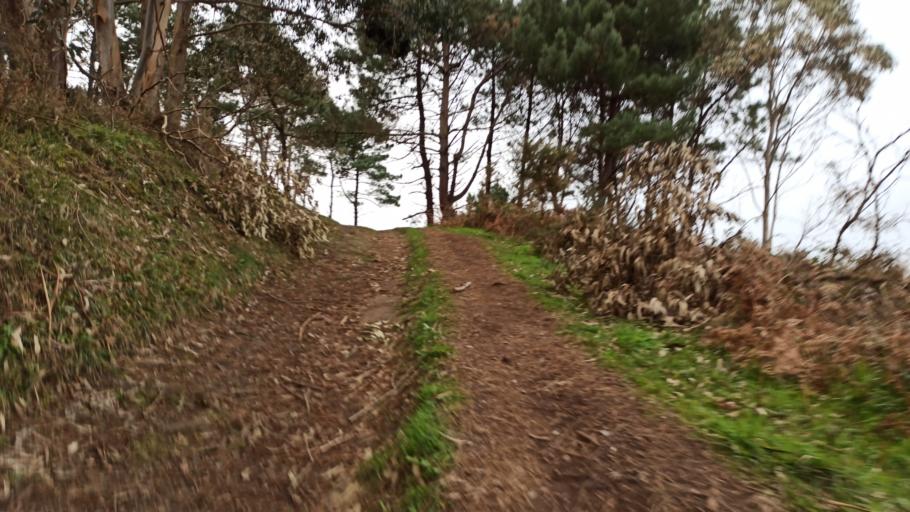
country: ES
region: Galicia
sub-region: Provincia da Coruna
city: A Coruna
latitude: 43.3966
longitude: -8.3353
